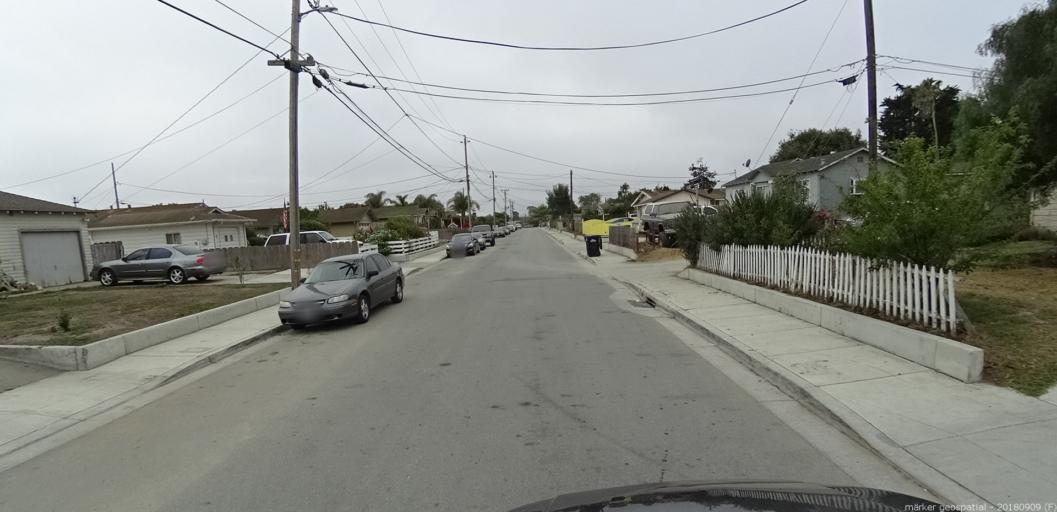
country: US
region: California
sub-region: Monterey County
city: Boronda
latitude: 36.7013
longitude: -121.6704
